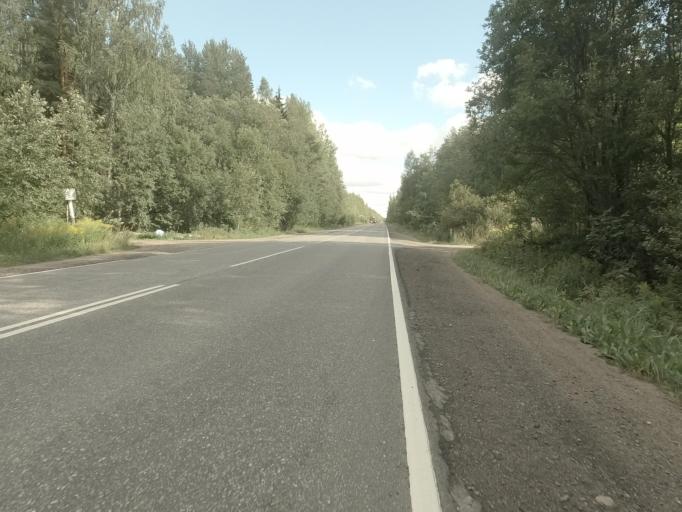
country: RU
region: Leningrad
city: Shcheglovo
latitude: 60.0052
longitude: 30.8647
